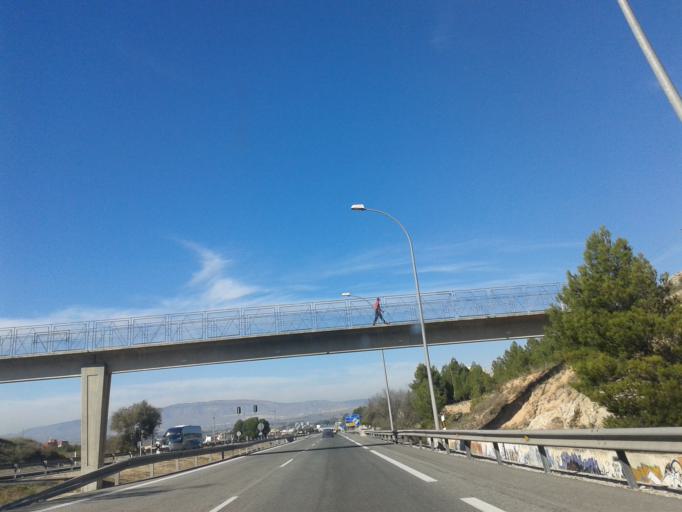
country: ES
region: Valencia
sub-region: Provincia de Alicante
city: Villena
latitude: 38.6381
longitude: -0.8593
